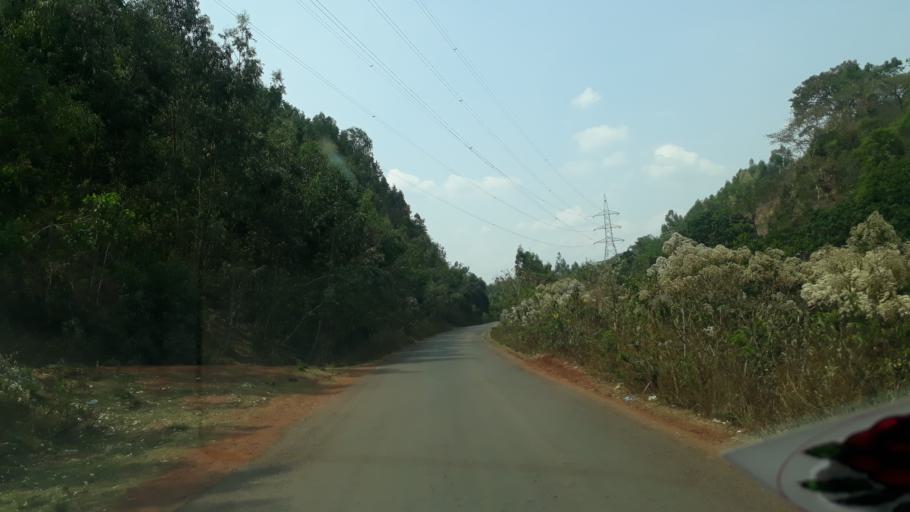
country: ET
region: Oromiya
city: Agaro
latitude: 7.9240
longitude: 36.5157
